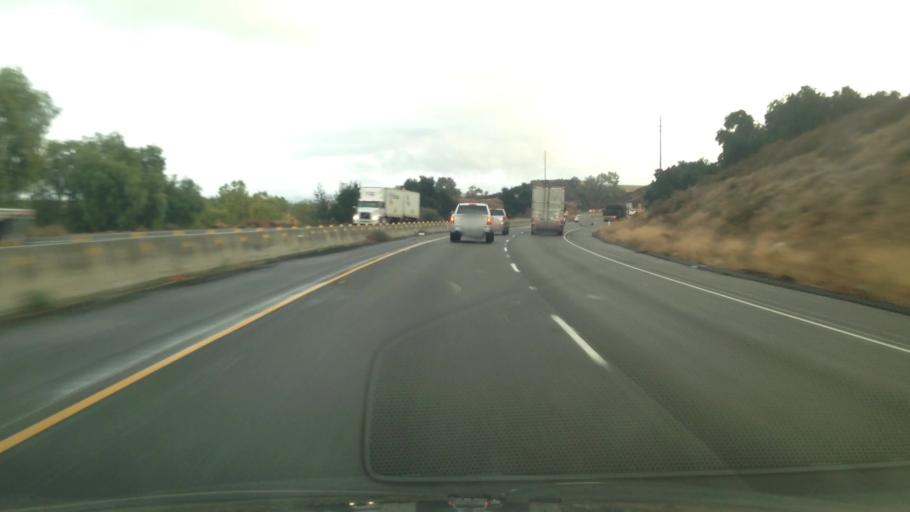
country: US
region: California
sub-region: Riverside County
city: Beaumont
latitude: 33.9387
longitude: -117.0409
